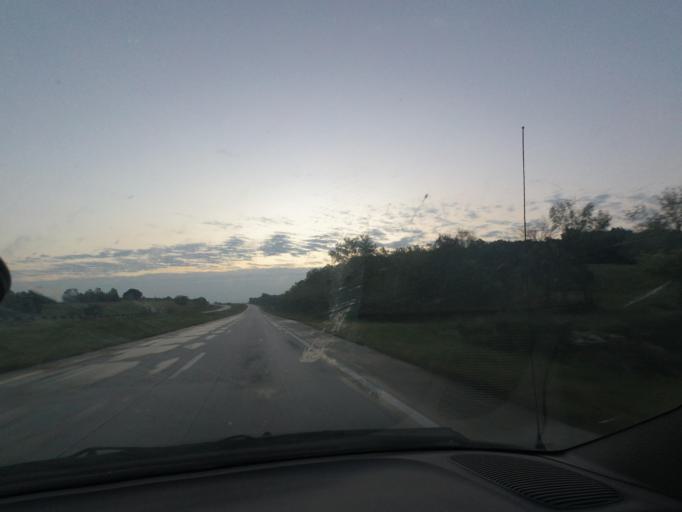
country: US
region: Missouri
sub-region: Linn County
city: Marceline
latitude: 39.7601
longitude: -92.8036
